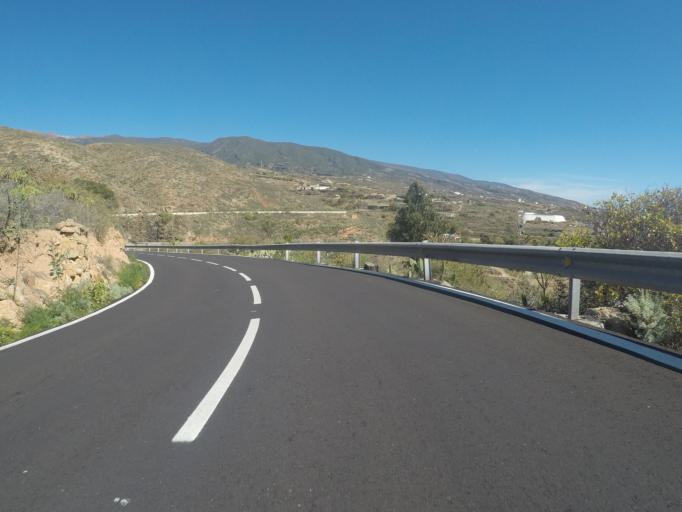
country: ES
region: Canary Islands
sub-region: Provincia de Santa Cruz de Tenerife
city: Lomo de Arico
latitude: 28.1695
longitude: -16.5009
